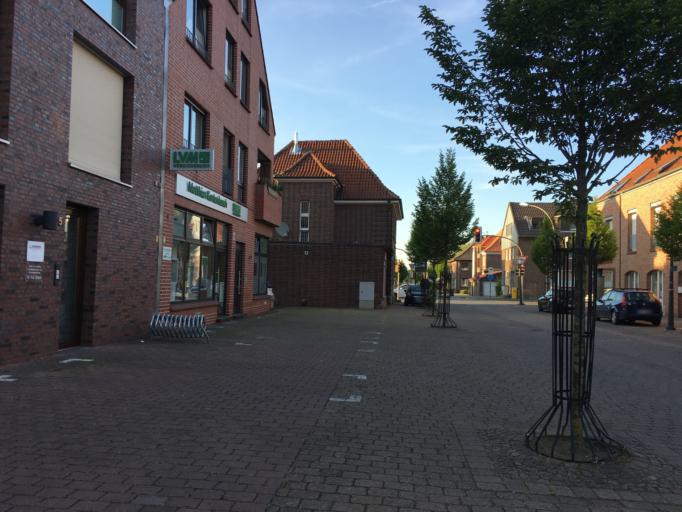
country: DE
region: North Rhine-Westphalia
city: Olfen
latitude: 51.7085
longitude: 7.3796
